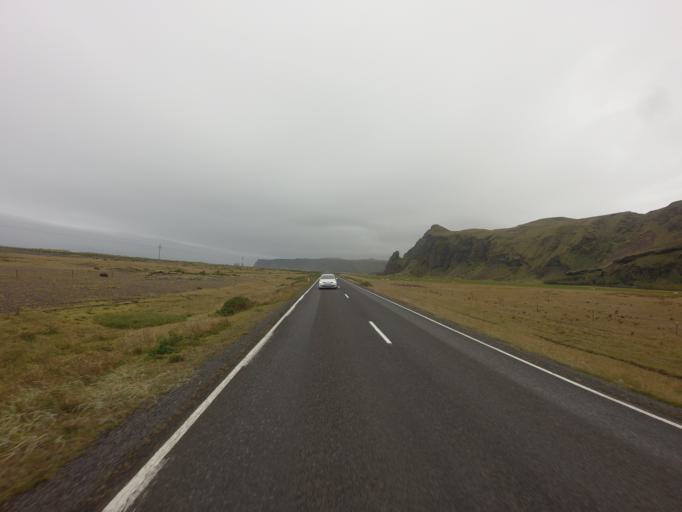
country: IS
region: South
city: Vestmannaeyjar
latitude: 63.4199
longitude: -18.9393
